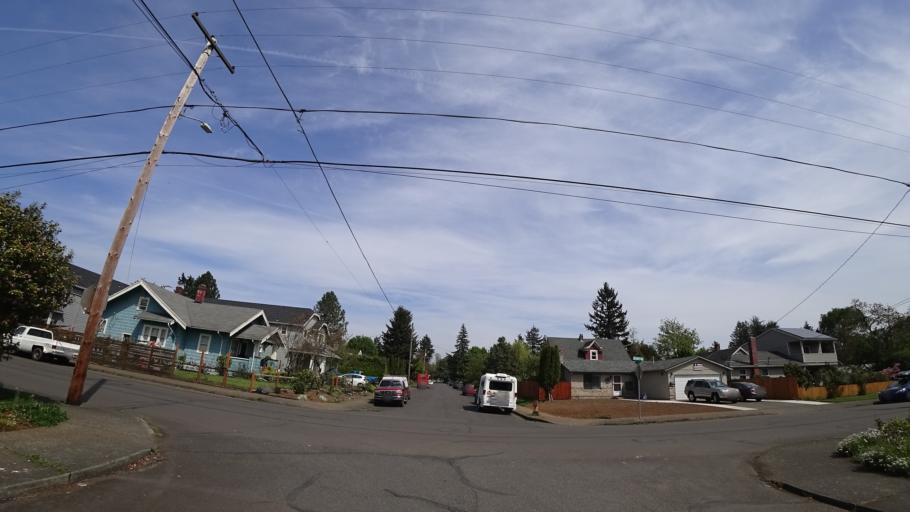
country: US
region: Oregon
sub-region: Multnomah County
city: Lents
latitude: 45.4783
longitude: -122.6024
